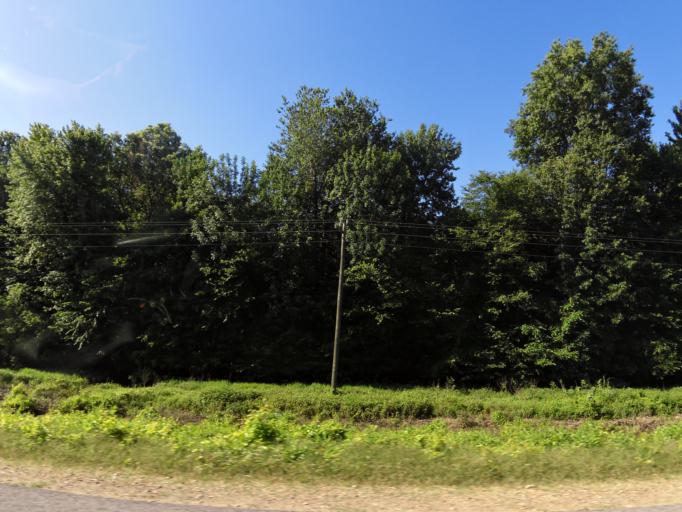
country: US
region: Arkansas
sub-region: Clay County
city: Corning
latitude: 36.4002
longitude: -90.5356
